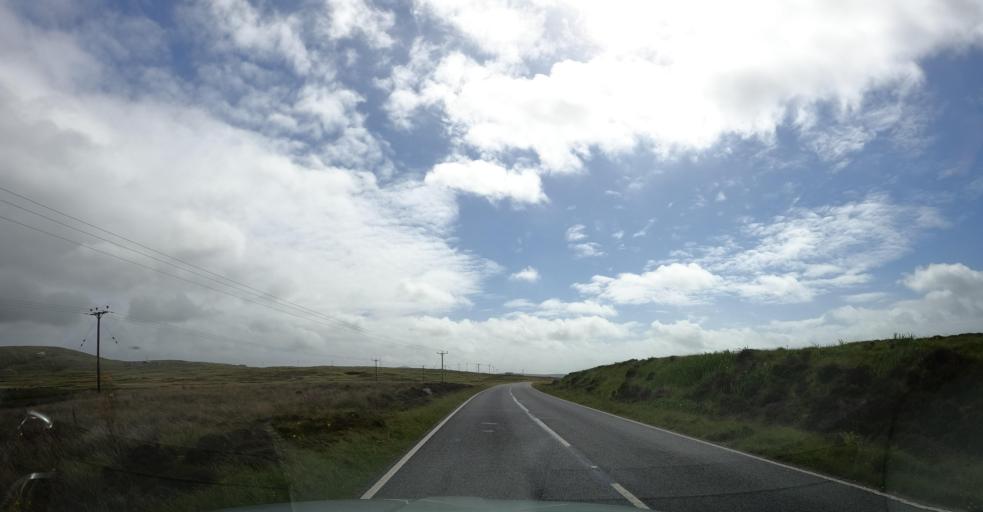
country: GB
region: Scotland
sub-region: Eilean Siar
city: Isle of South Uist
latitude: 57.2724
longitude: -7.3655
